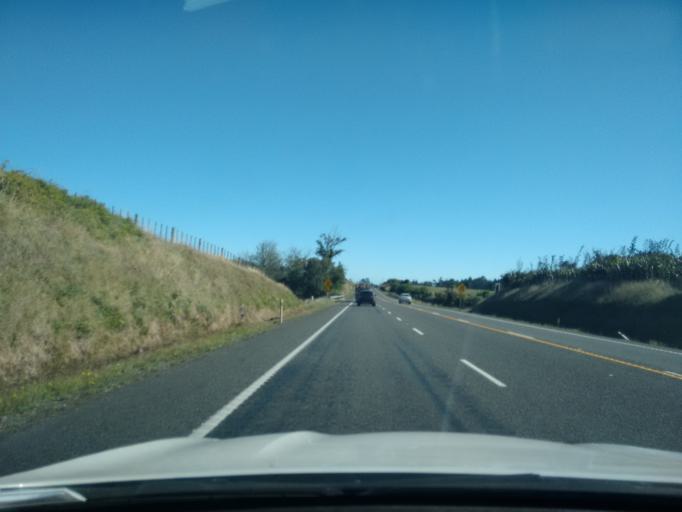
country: NZ
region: Taranaki
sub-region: New Plymouth District
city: New Plymouth
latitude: -39.1383
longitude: 174.1322
